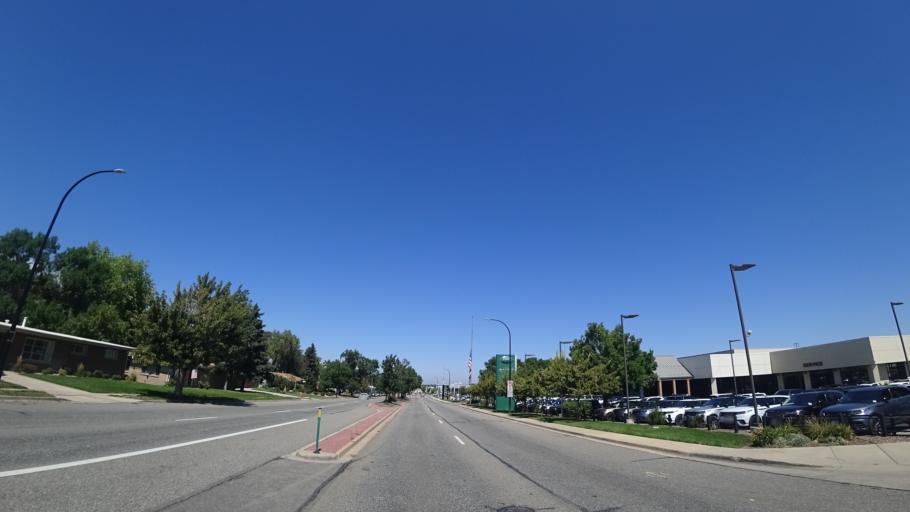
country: US
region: Colorado
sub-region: Arapahoe County
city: Littleton
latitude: 39.6038
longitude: -104.9880
